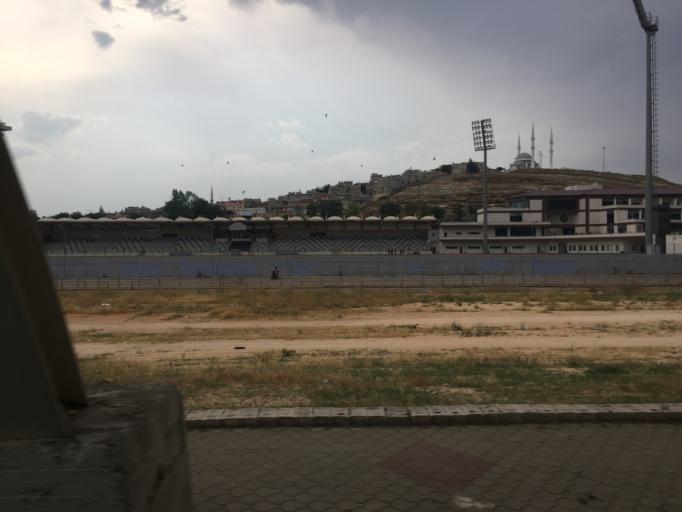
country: TR
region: Gaziantep
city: Gaziantep
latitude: 37.0752
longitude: 37.4132
